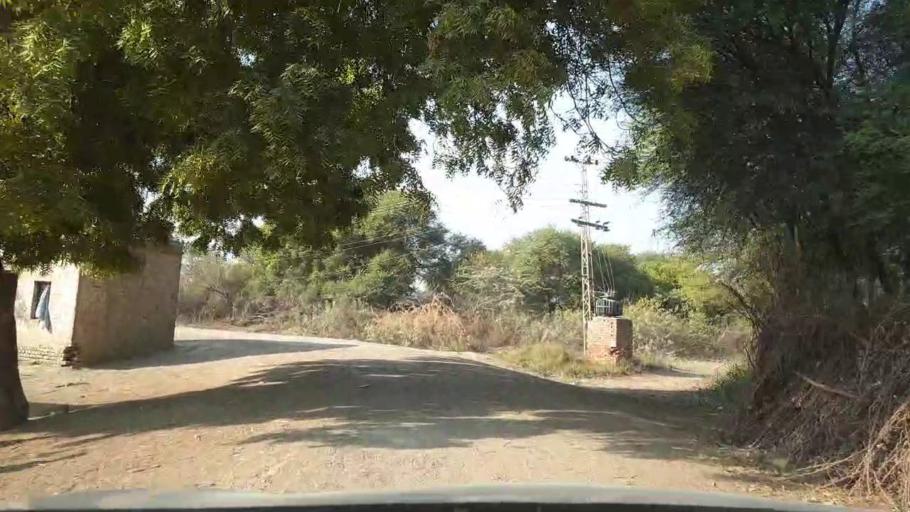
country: PK
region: Sindh
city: Tando Allahyar
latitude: 25.5667
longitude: 68.7637
